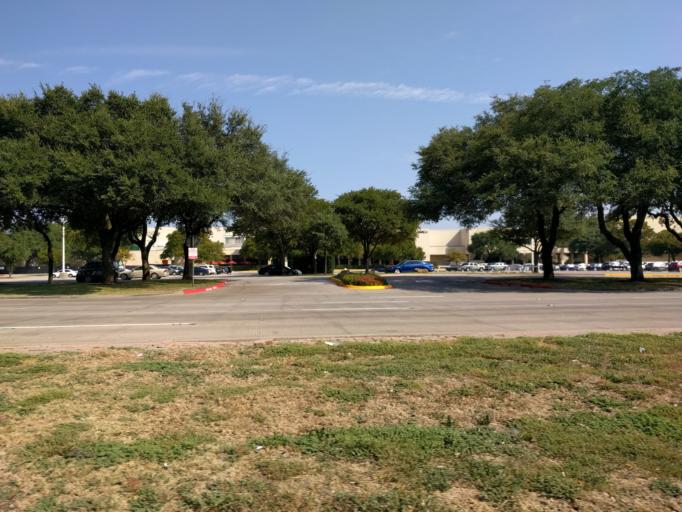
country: US
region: Texas
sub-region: Dallas County
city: University Park
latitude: 32.8654
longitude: -96.7734
